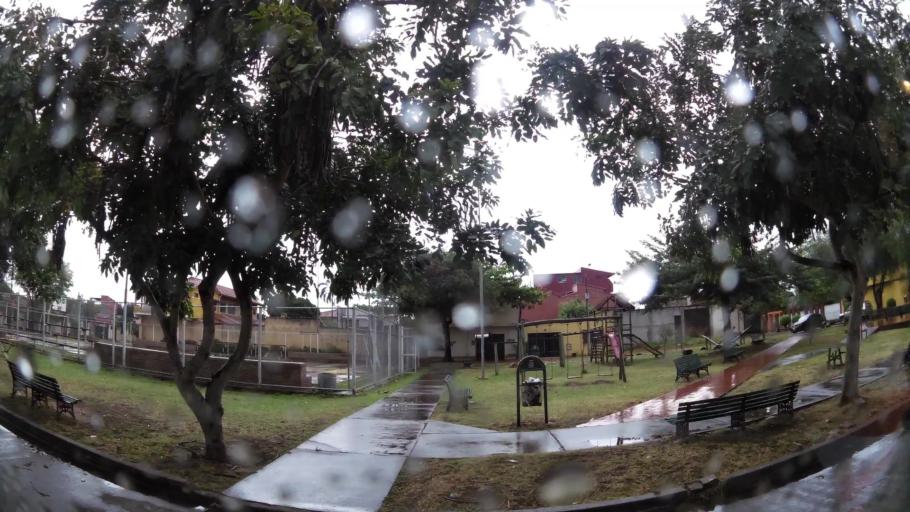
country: BO
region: Santa Cruz
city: Santa Cruz de la Sierra
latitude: -17.7957
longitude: -63.1534
